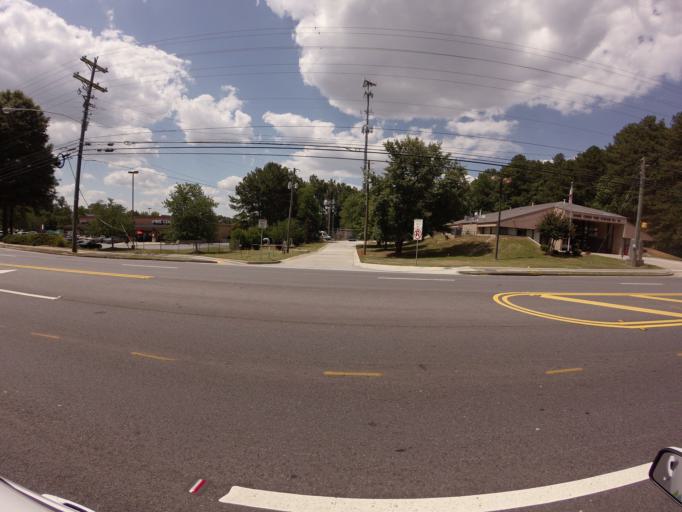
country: US
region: Georgia
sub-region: Fulton County
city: Alpharetta
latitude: 34.0212
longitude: -84.2673
